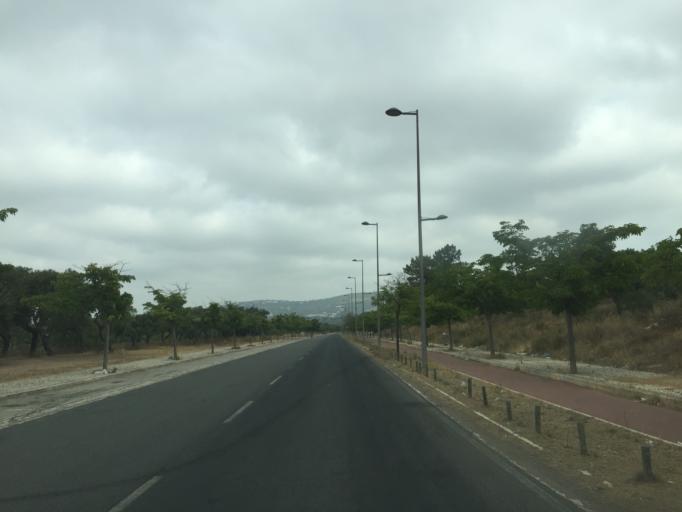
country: PT
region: Faro
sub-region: Faro
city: Santa Barbara de Nexe
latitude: 37.0787
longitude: -7.9762
